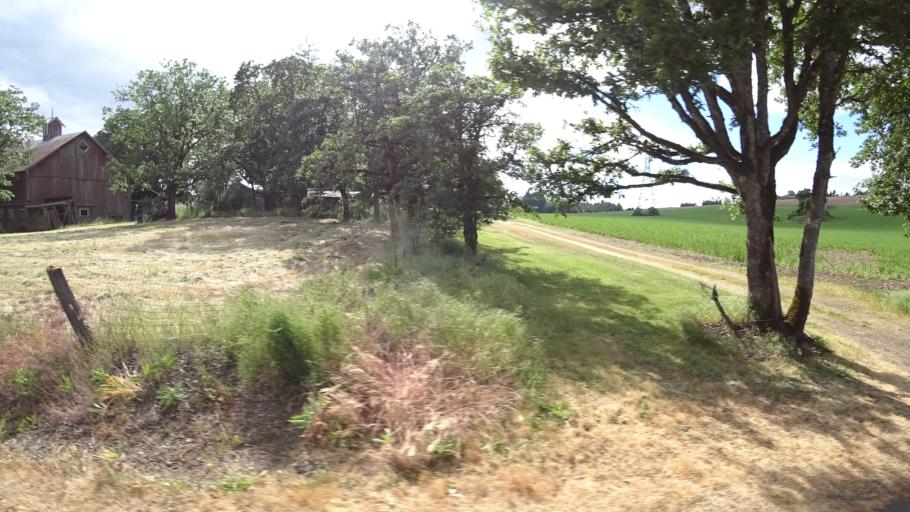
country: US
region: Oregon
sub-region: Washington County
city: Bethany
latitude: 45.5822
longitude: -122.8407
